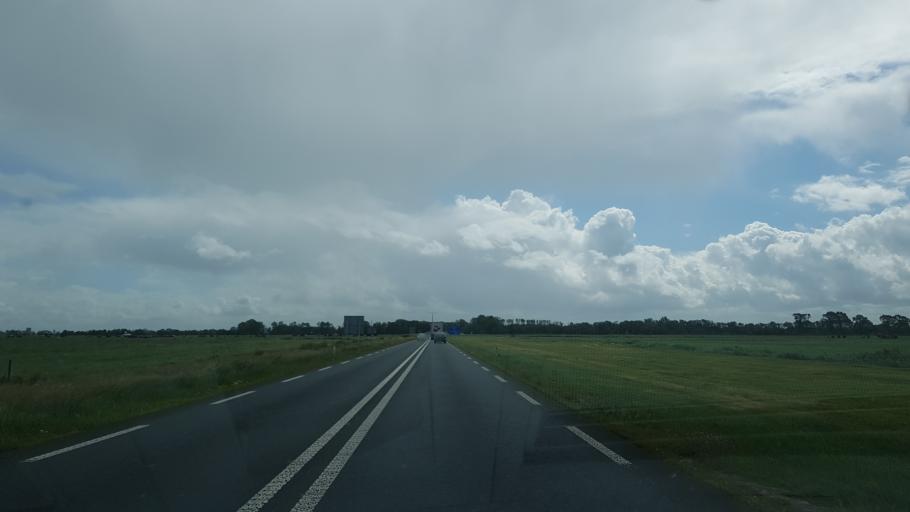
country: NL
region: Friesland
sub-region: Gemeente Dongeradeel
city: Dokkum
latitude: 53.3113
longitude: 6.0134
